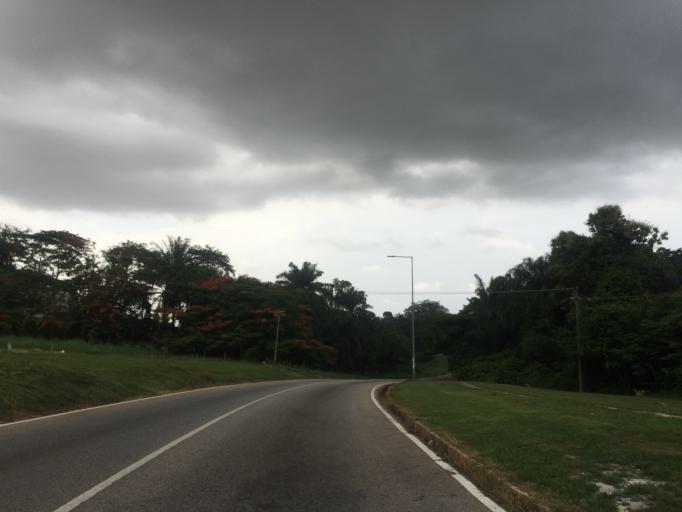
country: GH
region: Ashanti
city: Kumasi
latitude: 6.6794
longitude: -1.5708
